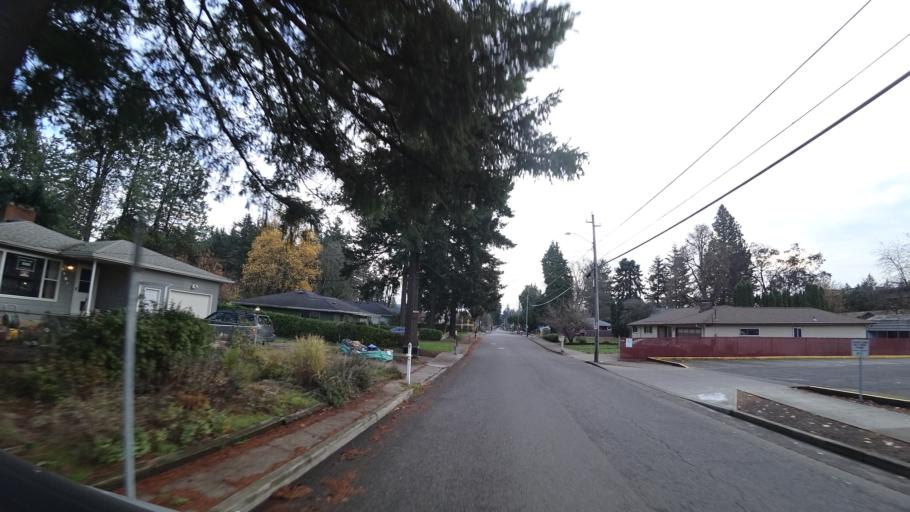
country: US
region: Oregon
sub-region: Multnomah County
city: Lents
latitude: 45.5155
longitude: -122.5248
